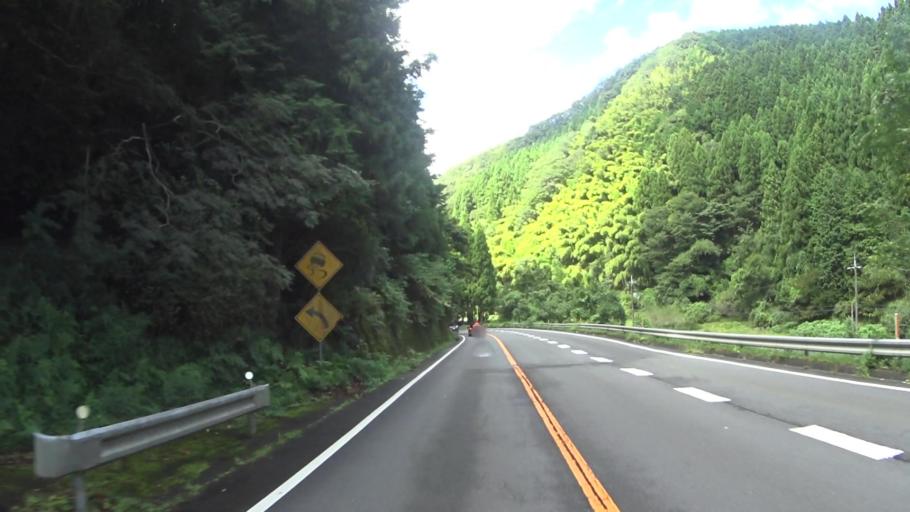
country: JP
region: Kyoto
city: Ayabe
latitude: 35.2440
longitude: 135.3094
